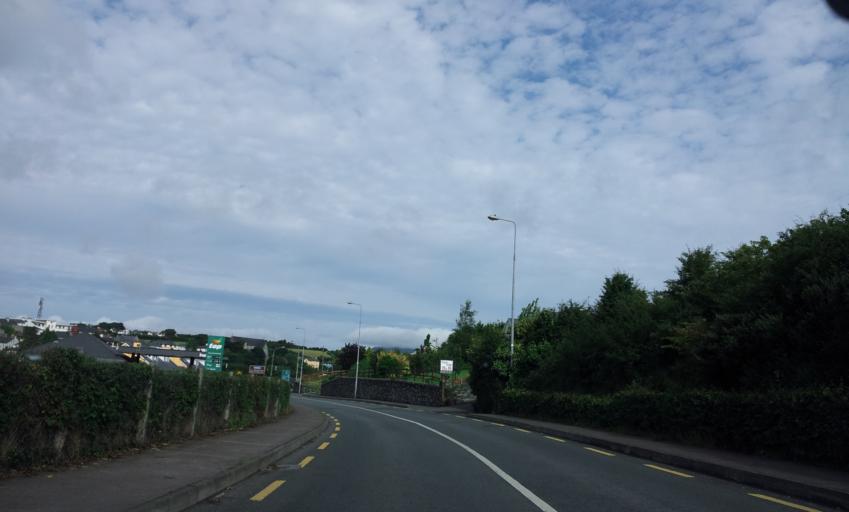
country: IE
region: Munster
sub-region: Ciarrai
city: Killorglin
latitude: 52.1044
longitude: -9.7792
